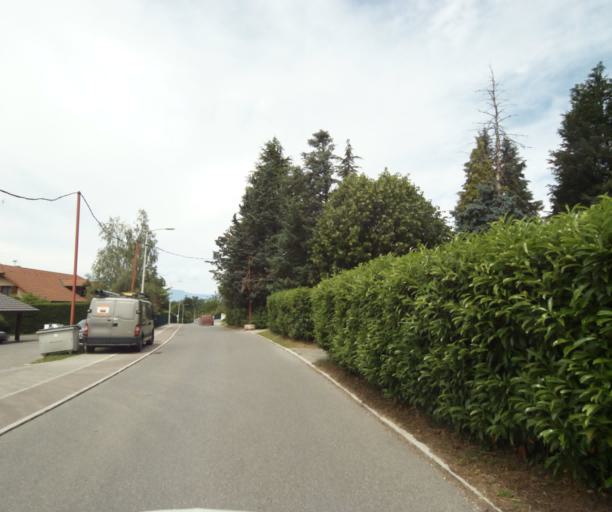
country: FR
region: Rhone-Alpes
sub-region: Departement de la Haute-Savoie
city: Anthy-sur-Leman
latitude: 46.3449
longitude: 6.4132
